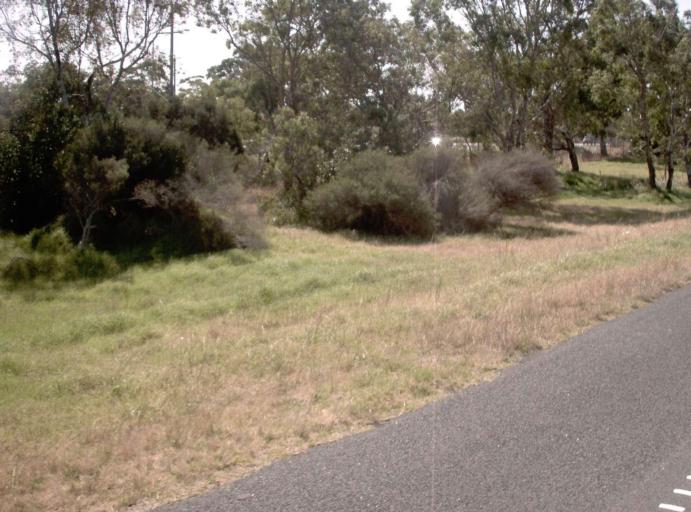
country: AU
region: Victoria
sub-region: Kingston
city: Chelsea Heights
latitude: -38.0491
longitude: 145.1434
